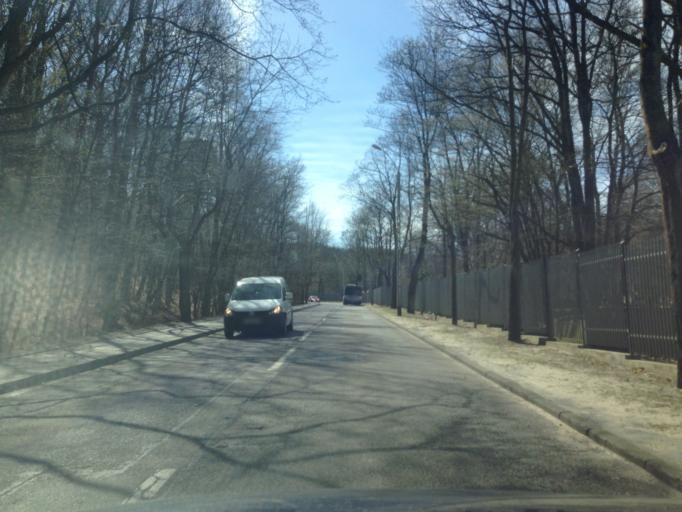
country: PL
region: Pomeranian Voivodeship
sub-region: Gdynia
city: Gdynia
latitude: 54.5086
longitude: 18.5177
